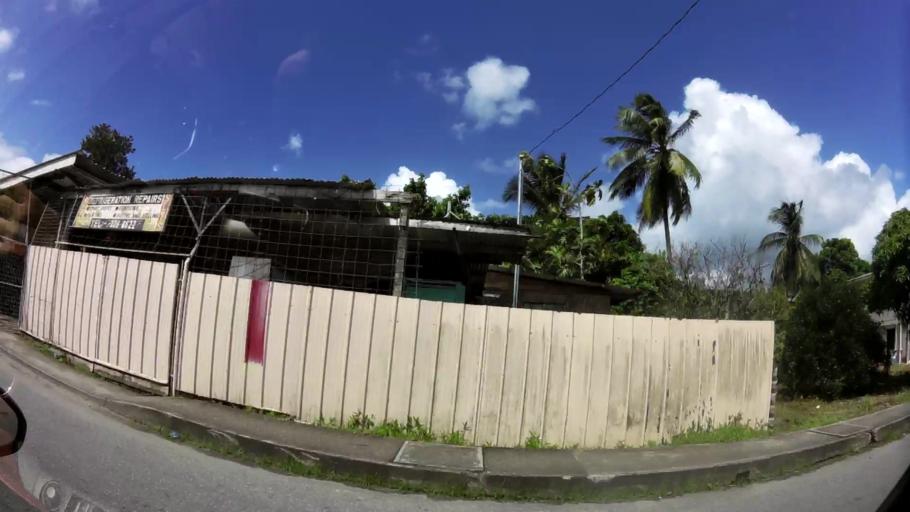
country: TT
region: Borough of Arima
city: Arima
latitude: 10.6309
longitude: -61.2783
